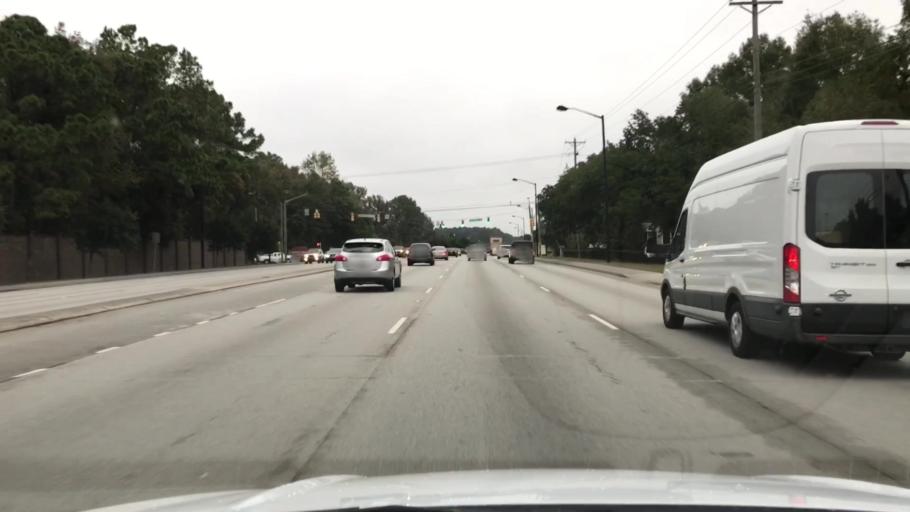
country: US
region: South Carolina
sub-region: Charleston County
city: Isle of Palms
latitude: 32.8436
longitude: -79.8150
